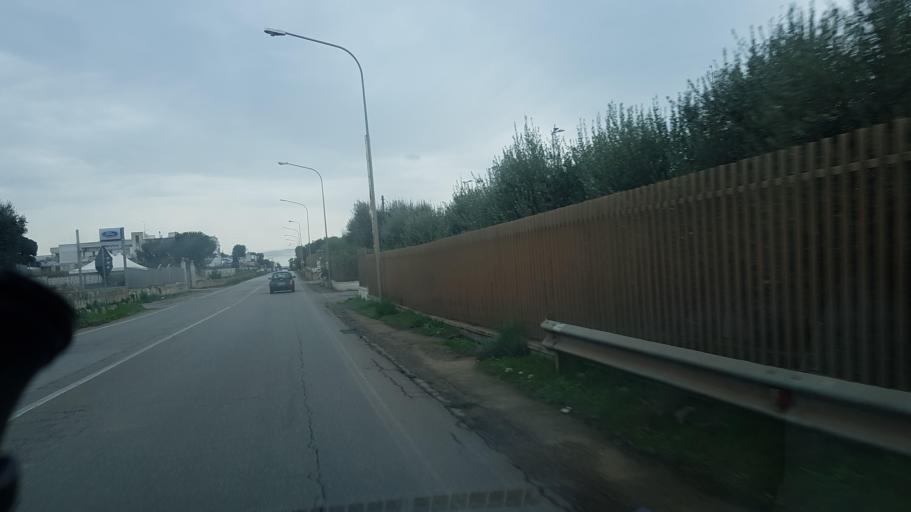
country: IT
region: Apulia
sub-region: Provincia di Brindisi
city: Ostuni
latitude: 40.7219
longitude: 17.6026
